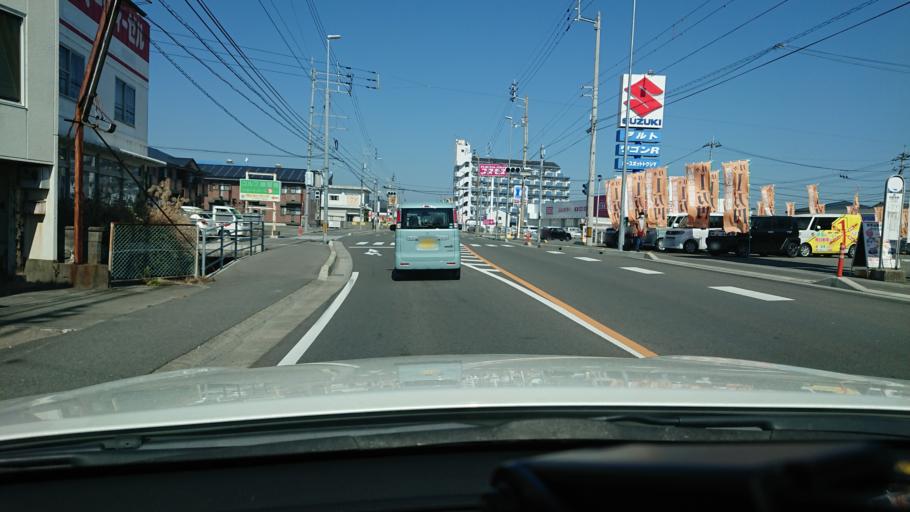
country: JP
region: Tokushima
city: Narutocho-mitsuishi
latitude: 34.1440
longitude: 134.5936
